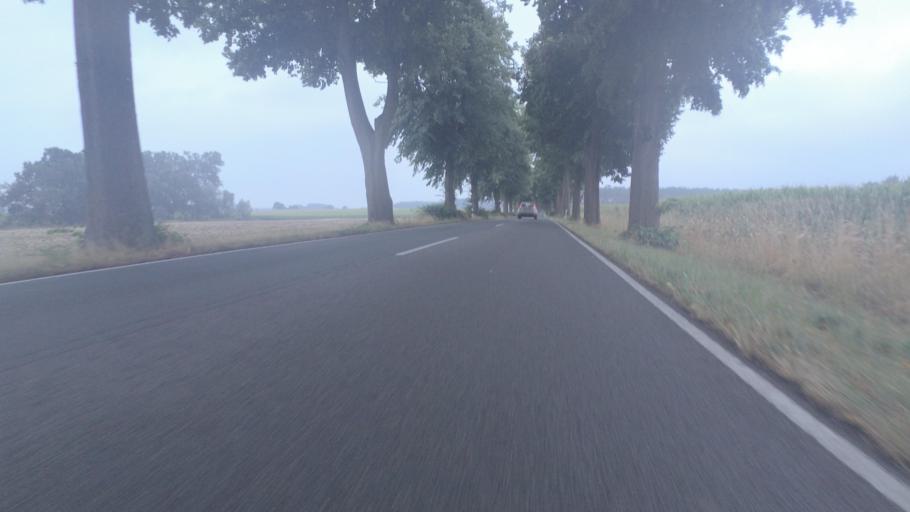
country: DE
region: Brandenburg
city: Heiligengrabe
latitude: 53.1129
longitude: 12.3728
